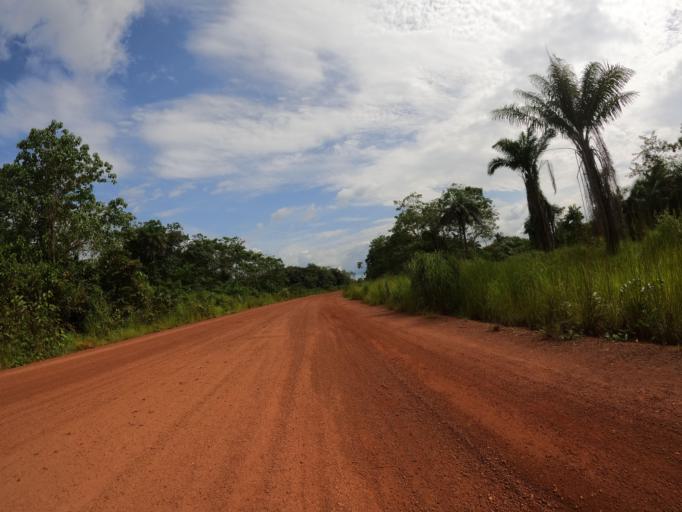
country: SL
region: Northern Province
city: Binkolo
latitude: 9.1514
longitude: -12.2166
